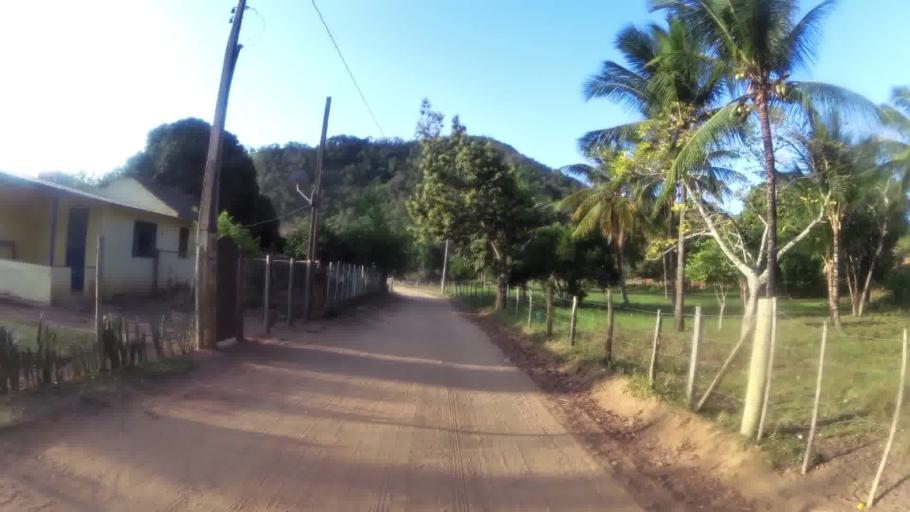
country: BR
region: Espirito Santo
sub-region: Piuma
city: Piuma
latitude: -20.8847
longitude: -40.7826
